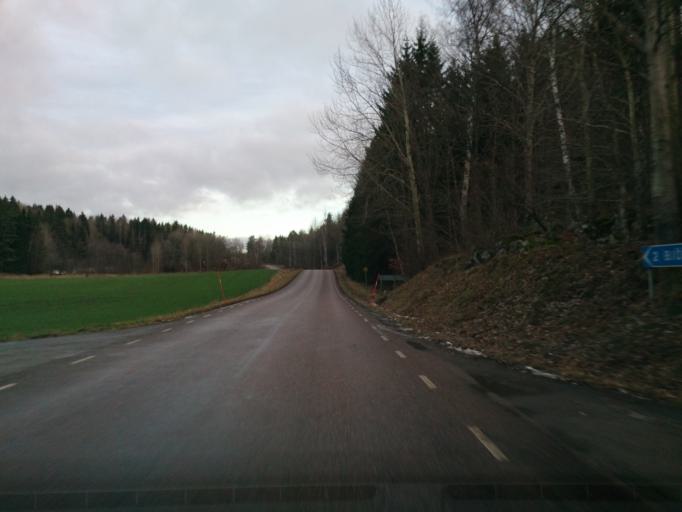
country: SE
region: OEstergoetland
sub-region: Atvidabergs Kommun
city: Atvidaberg
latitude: 58.3148
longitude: 16.0263
